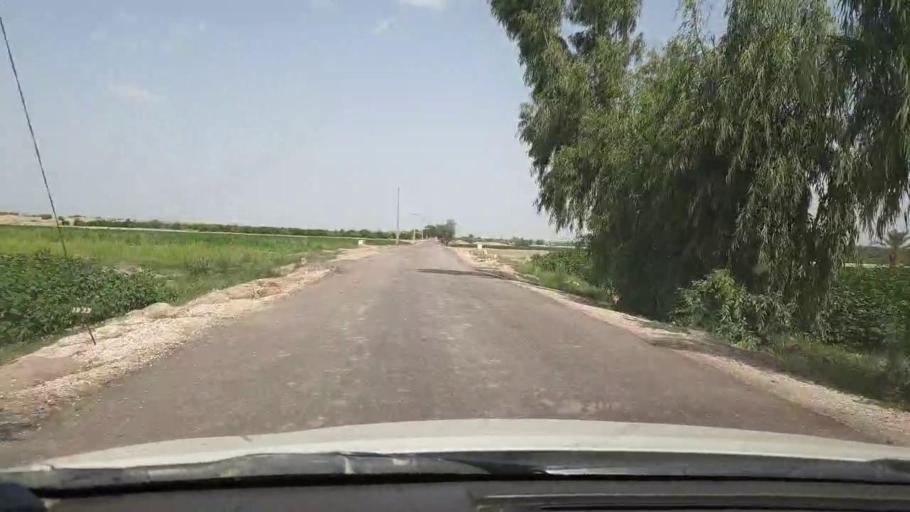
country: PK
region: Sindh
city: Rohri
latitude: 27.4821
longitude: 69.0650
